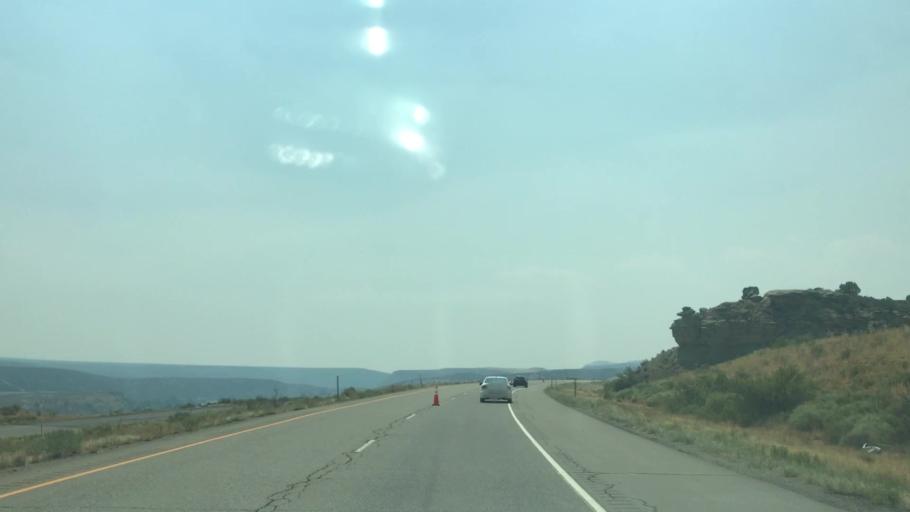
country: US
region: Colorado
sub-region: Garfield County
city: Parachute
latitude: 39.3921
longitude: -108.1297
